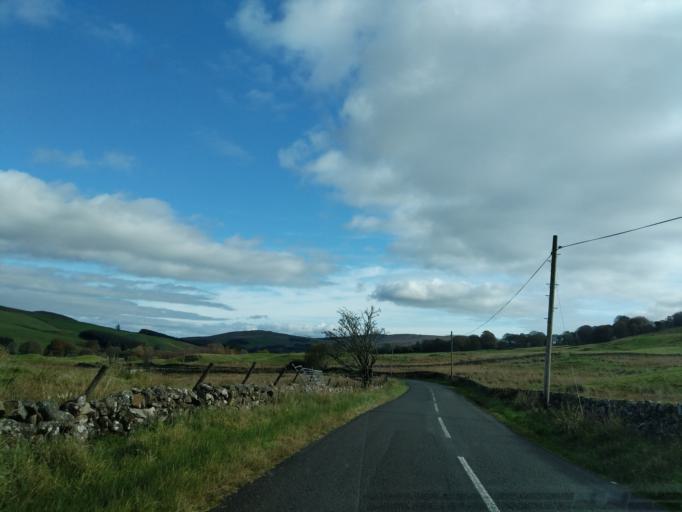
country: GB
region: Scotland
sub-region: Dumfries and Galloway
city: Sanquhar
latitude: 55.1574
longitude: -4.0030
